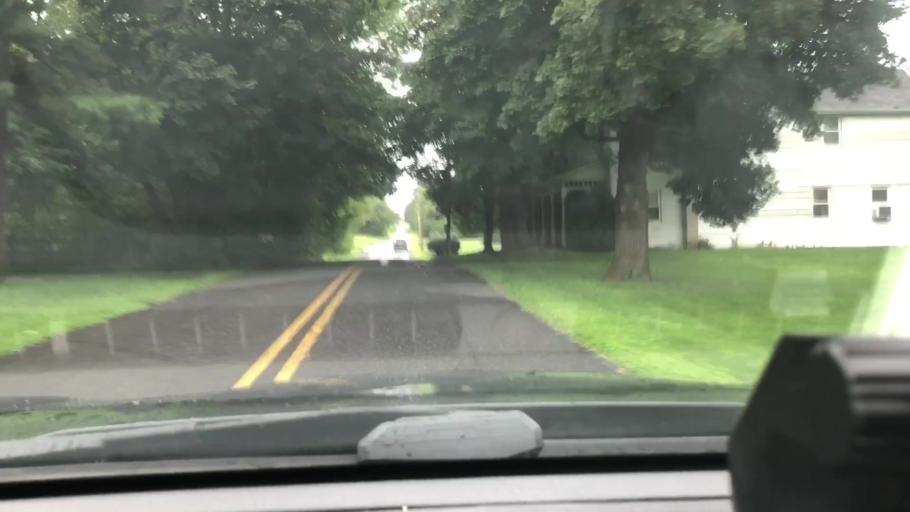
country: US
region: Pennsylvania
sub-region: Lehigh County
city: Coopersburg
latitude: 40.4849
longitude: -75.4042
